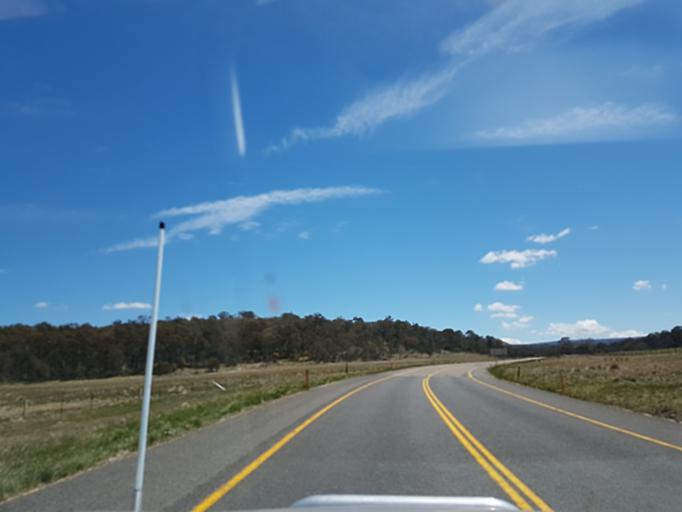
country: AU
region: Victoria
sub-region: Alpine
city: Mount Beauty
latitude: -37.0568
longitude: 147.3268
